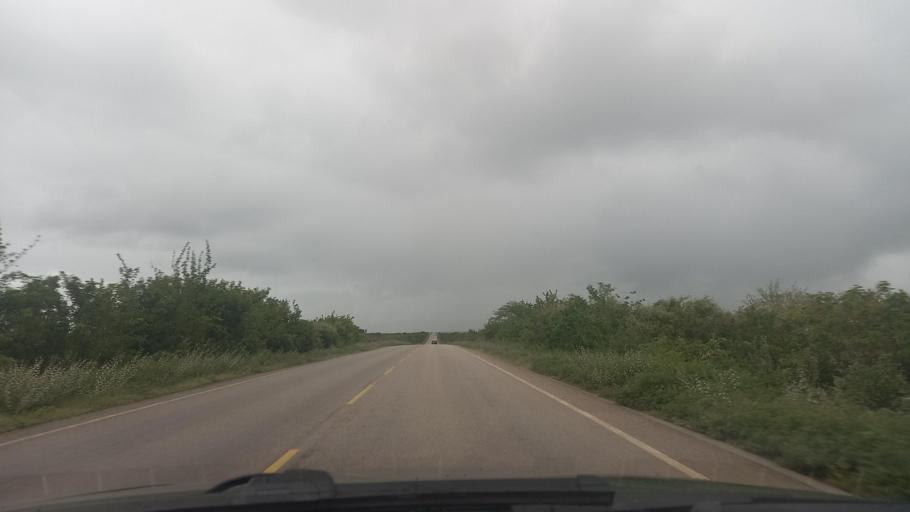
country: BR
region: Bahia
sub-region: Paulo Afonso
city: Paulo Afonso
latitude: -9.3326
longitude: -38.2858
